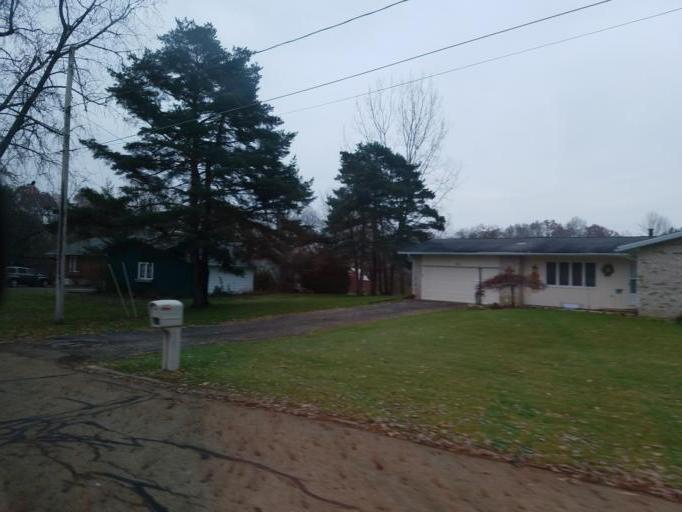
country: US
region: Ohio
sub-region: Richland County
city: Lexington
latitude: 40.7020
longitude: -82.5342
